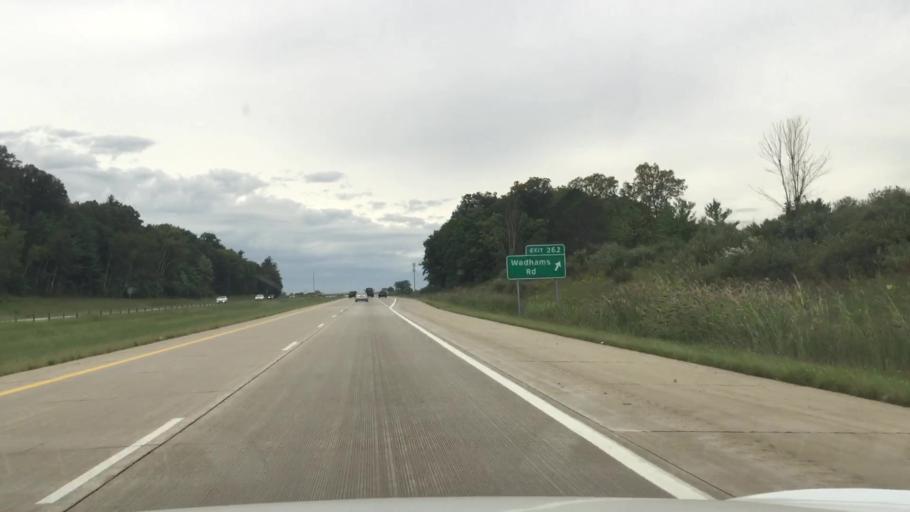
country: US
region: Michigan
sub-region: Saint Clair County
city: Marysville
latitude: 42.8685
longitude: -82.5492
